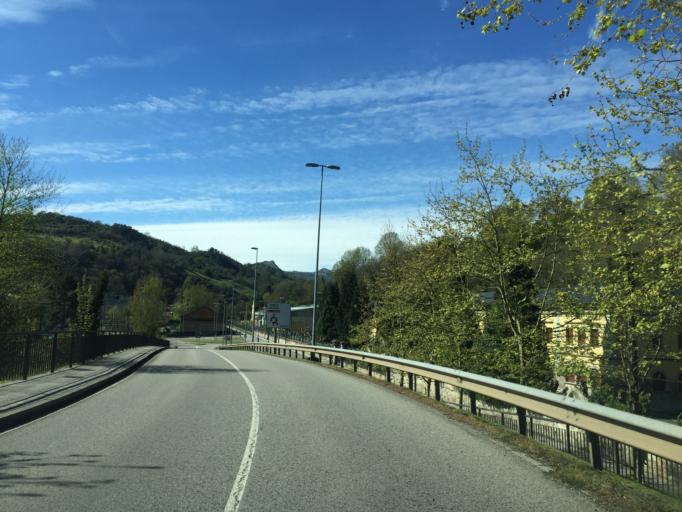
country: ES
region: Asturias
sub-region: Province of Asturias
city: Castandiello
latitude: 43.3523
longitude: -5.9679
